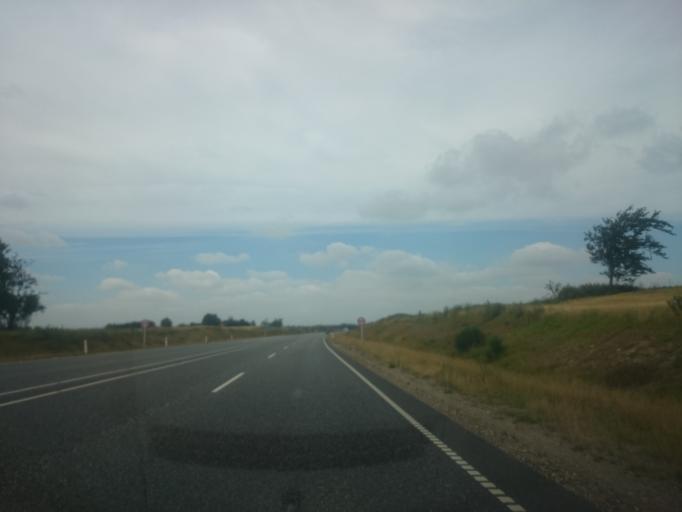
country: DK
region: South Denmark
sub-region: Vejle Kommune
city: Egtved
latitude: 55.6975
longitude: 9.3164
